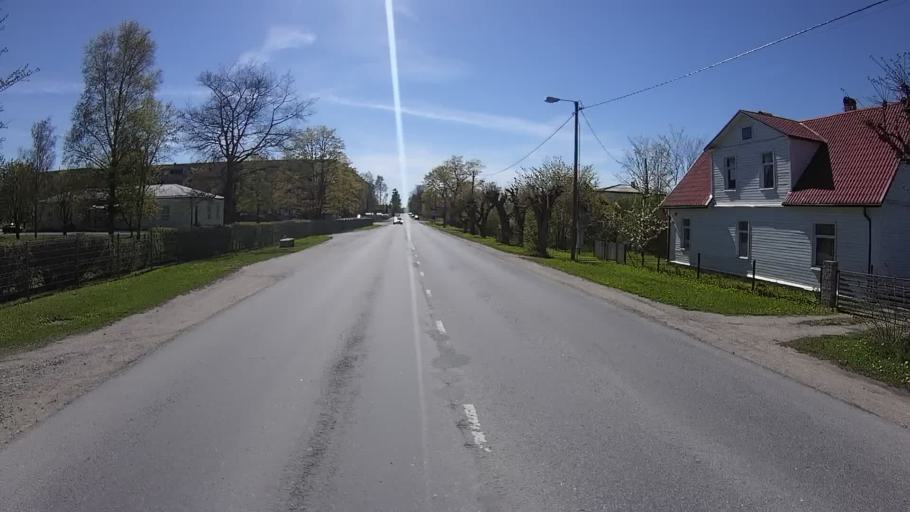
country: EE
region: Laeaene-Virumaa
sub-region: Tapa vald
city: Tapa
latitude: 59.2702
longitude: 25.9644
